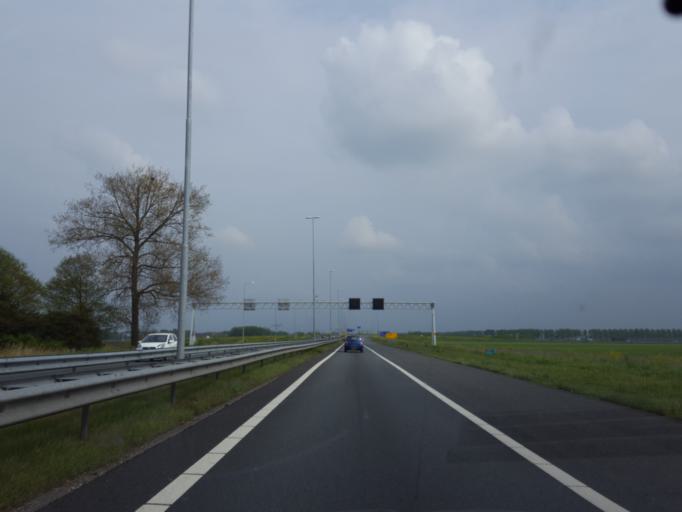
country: NL
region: Gelderland
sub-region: Gemeente Wijchen
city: Bergharen
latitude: 51.8623
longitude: 5.6993
